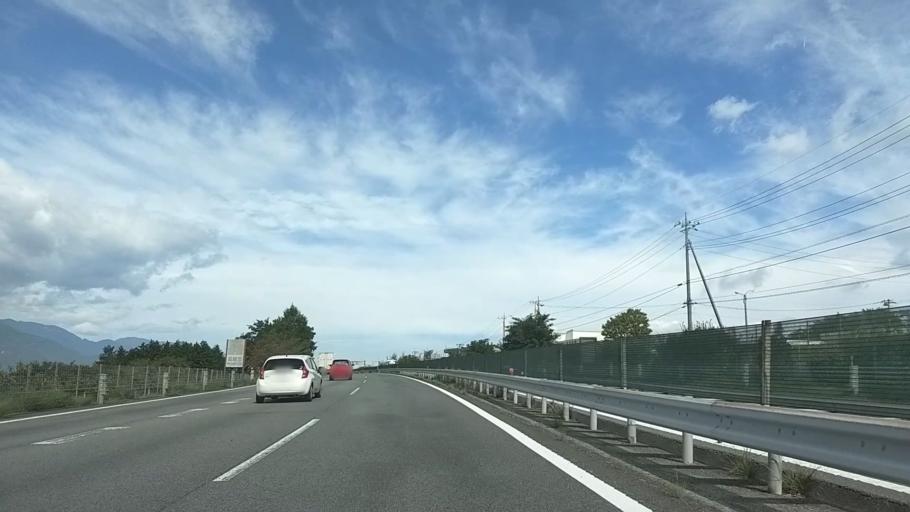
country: JP
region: Yamanashi
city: Nirasaki
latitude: 35.7130
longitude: 138.4717
